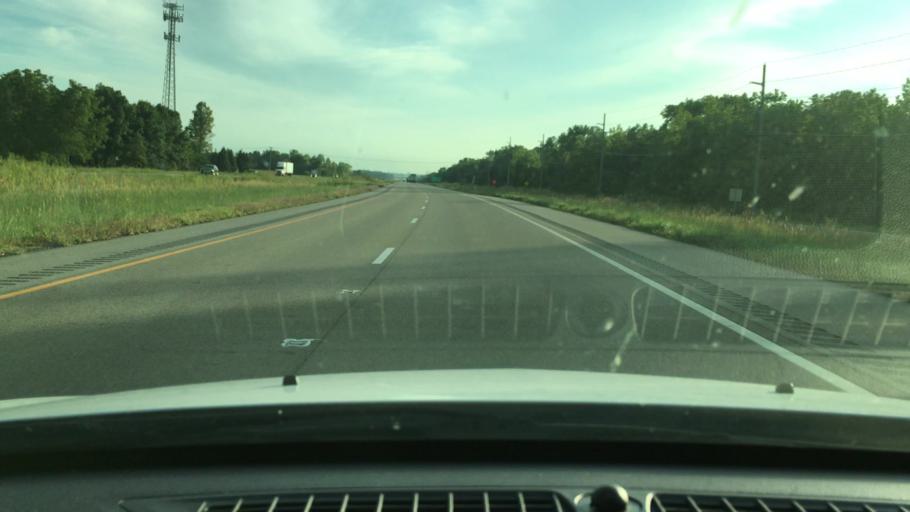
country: US
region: Illinois
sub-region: Logan County
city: Atlanta
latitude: 40.2476
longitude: -89.2472
